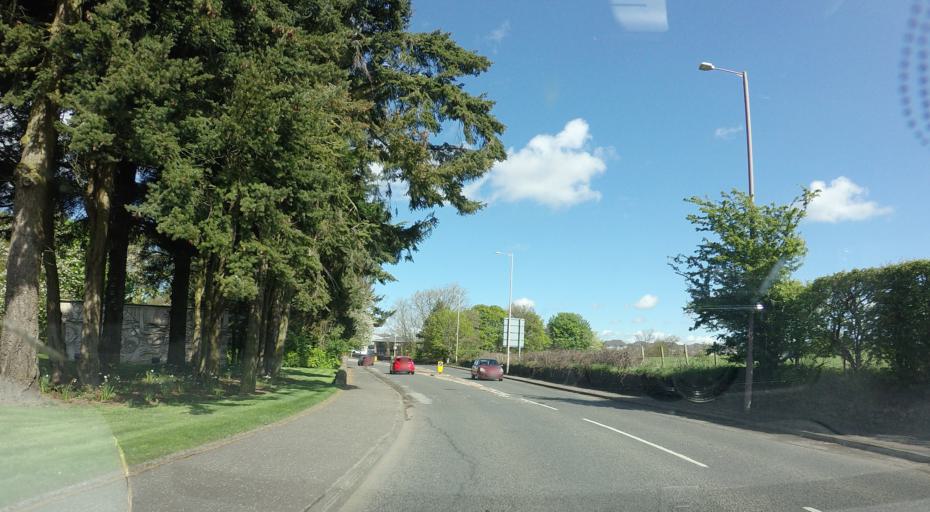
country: GB
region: Scotland
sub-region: Stirling
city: Bannockburn
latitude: 56.0846
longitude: -3.9269
